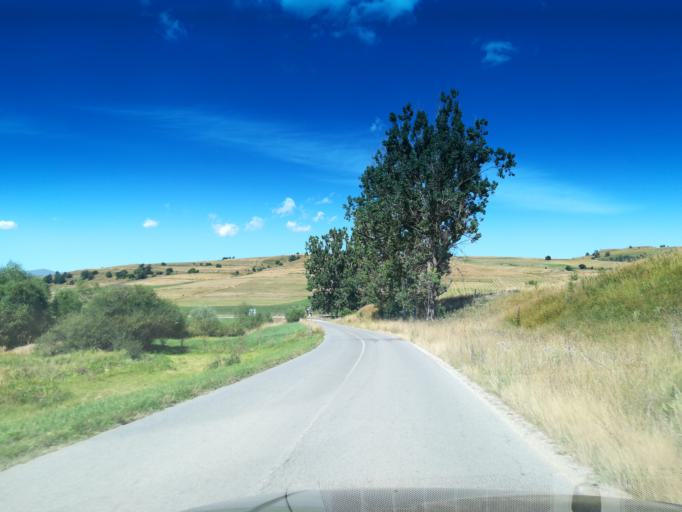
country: BG
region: Sofiya
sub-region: Obshtina Koprivshtitsa
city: Koprivshtitsa
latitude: 42.6022
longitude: 24.3803
